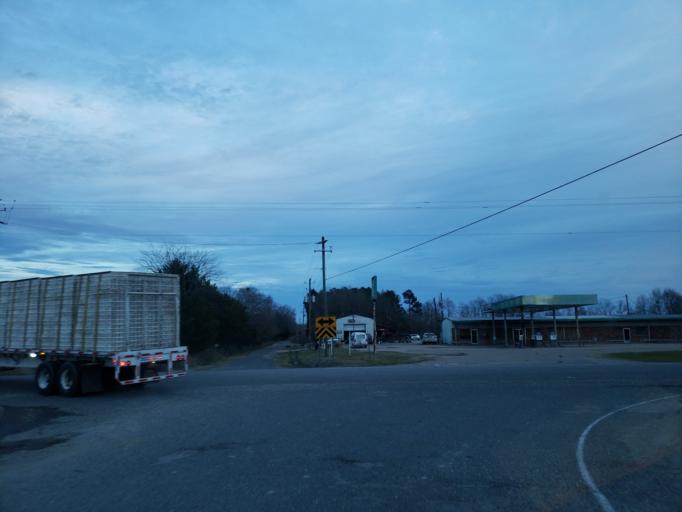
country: US
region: Alabama
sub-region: Sumter County
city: Livingston
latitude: 32.8317
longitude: -88.3094
